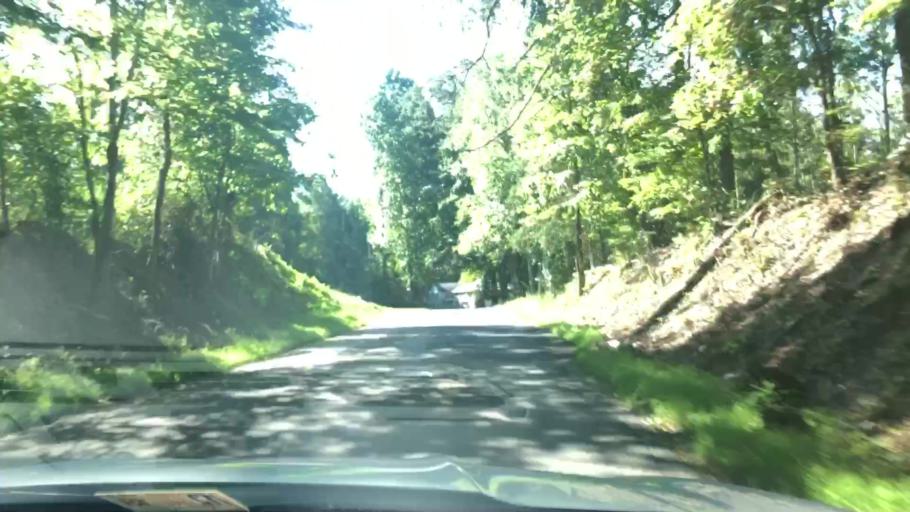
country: US
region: Virginia
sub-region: New Kent County
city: New Kent
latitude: 37.4777
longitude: -76.9333
